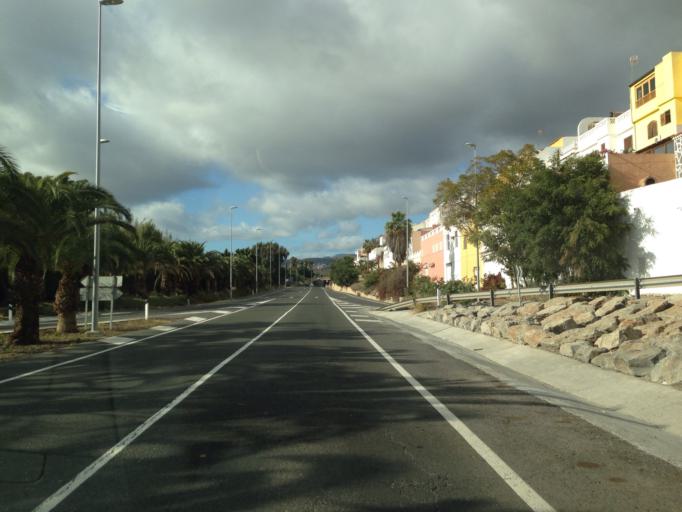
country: ES
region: Canary Islands
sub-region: Provincia de Las Palmas
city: Maspalomas
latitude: 27.7638
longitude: -15.5875
